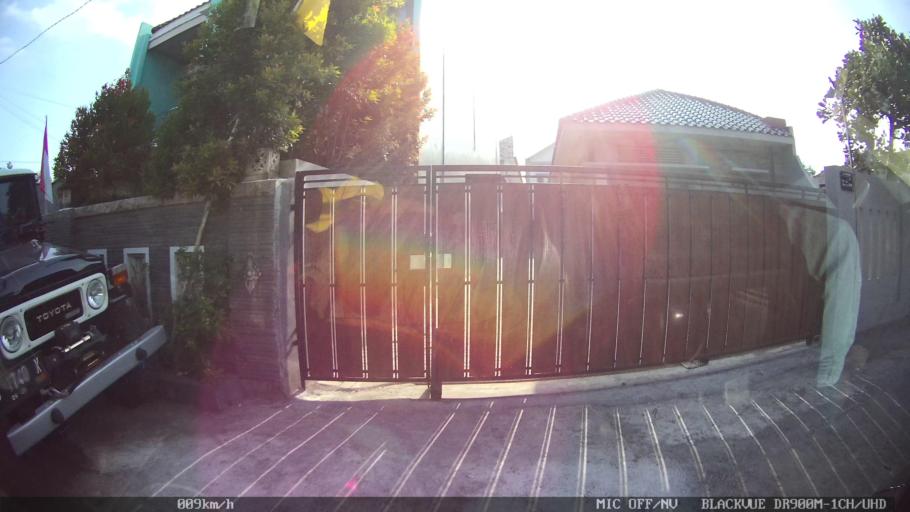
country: ID
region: Daerah Istimewa Yogyakarta
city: Yogyakarta
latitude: -7.8242
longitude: 110.3825
